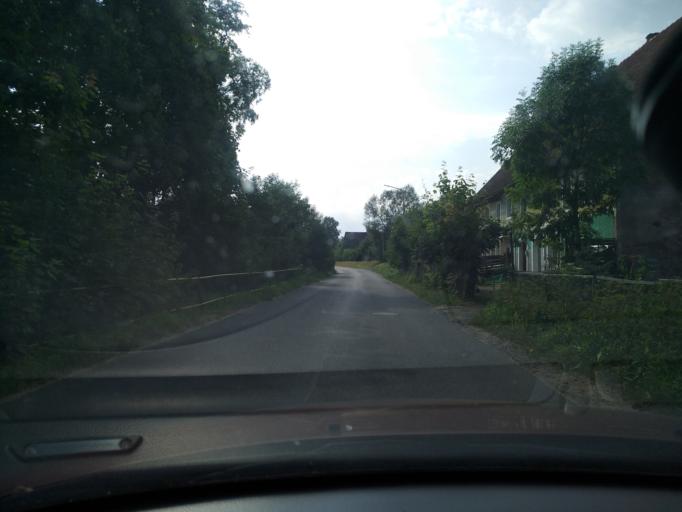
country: PL
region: Lower Silesian Voivodeship
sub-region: Powiat jeleniogorski
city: Stara Kamienica
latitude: 50.9035
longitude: 15.5684
